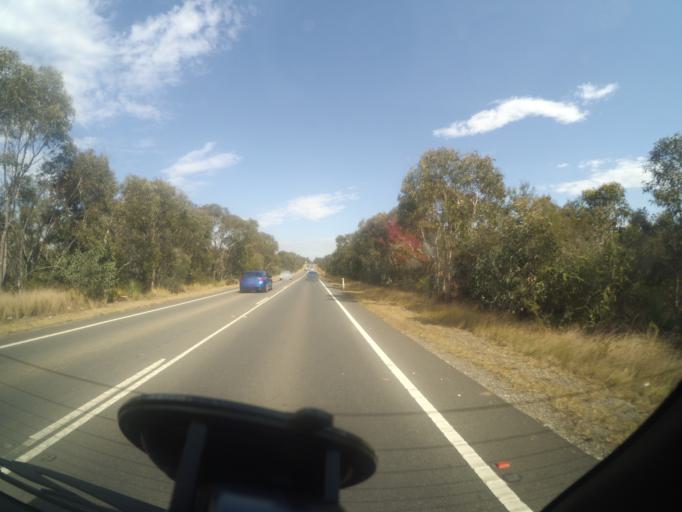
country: AU
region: New South Wales
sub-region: Sutherland Shire
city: Menai
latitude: -34.0076
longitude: 150.9899
